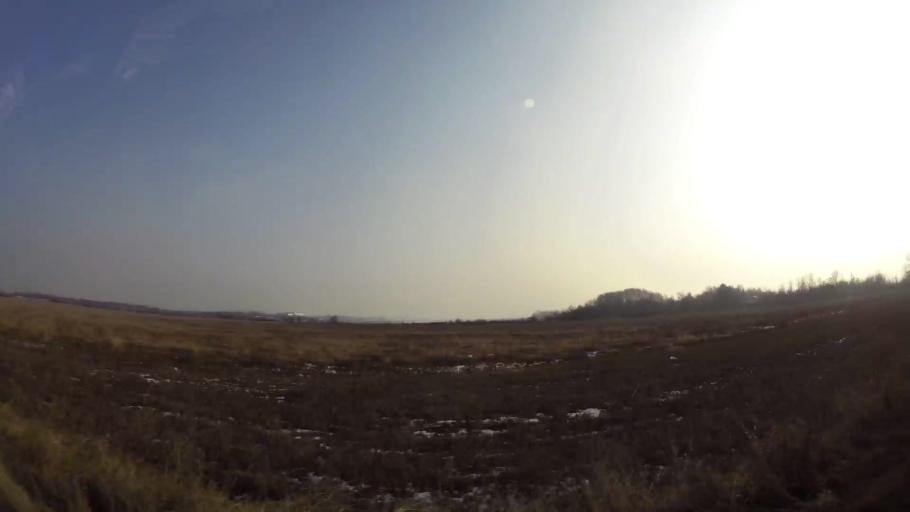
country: MK
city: Kadino
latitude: 41.9790
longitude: 21.6139
